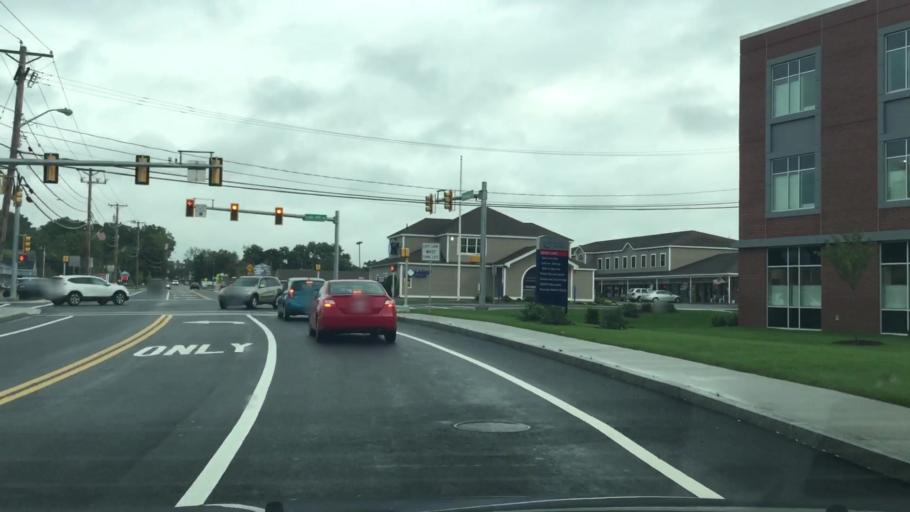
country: US
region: Massachusetts
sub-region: Middlesex County
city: Dracut
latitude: 42.6709
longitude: -71.2975
